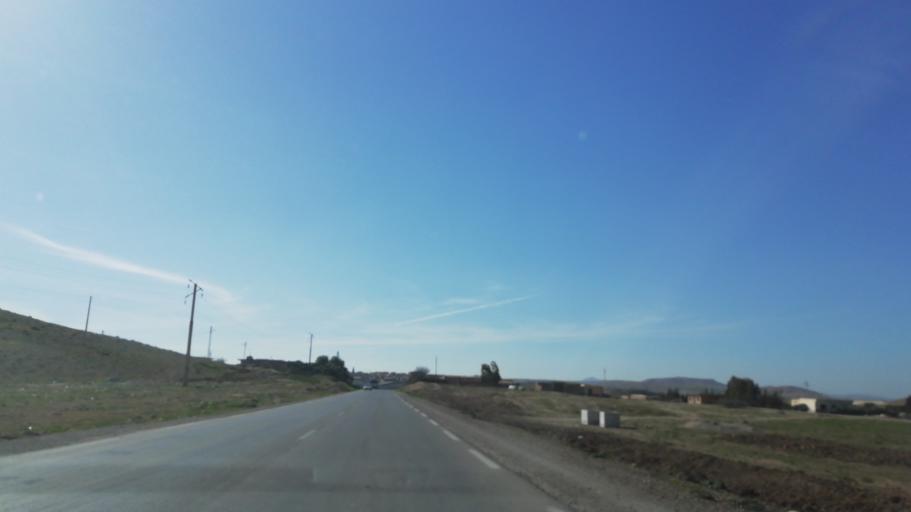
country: DZ
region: Mascara
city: Oued el Abtal
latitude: 35.4555
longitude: 0.7281
